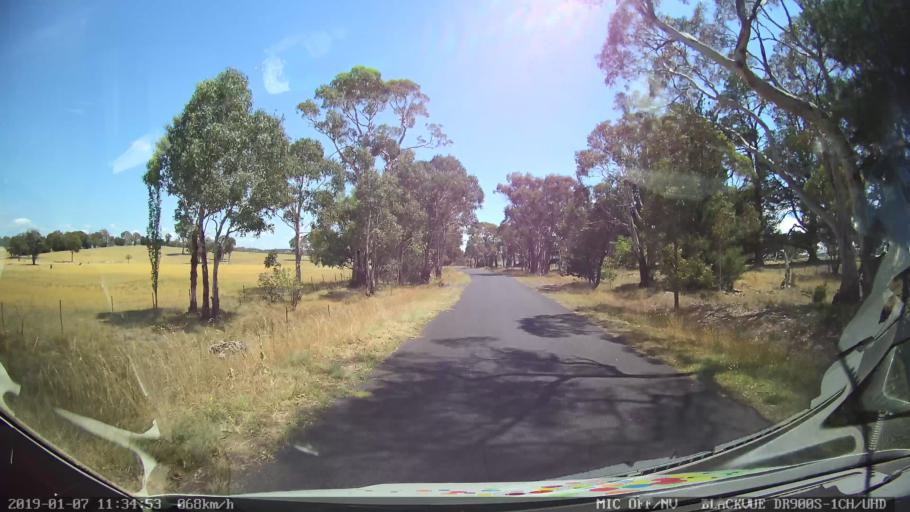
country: AU
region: New South Wales
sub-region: Armidale Dumaresq
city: Armidale
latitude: -30.3857
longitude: 151.5575
